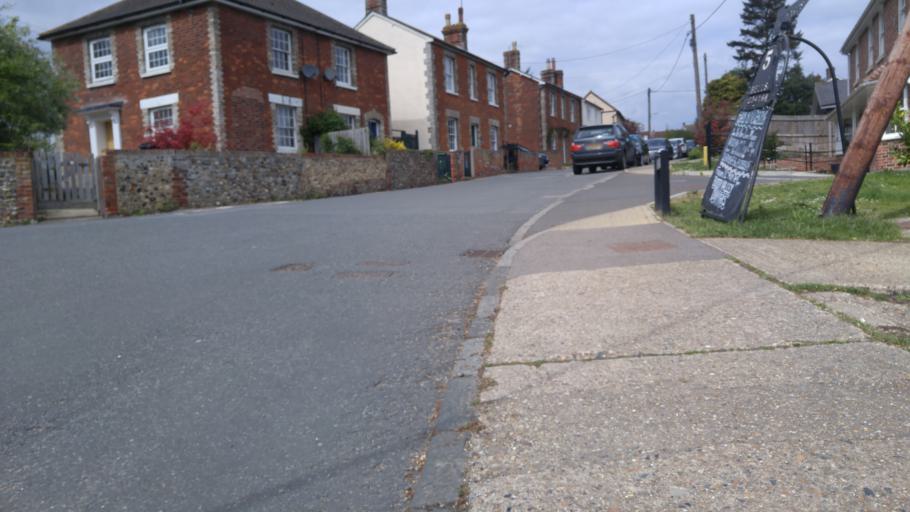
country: GB
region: England
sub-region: Essex
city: Earls Colne
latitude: 51.9411
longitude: 0.6912
